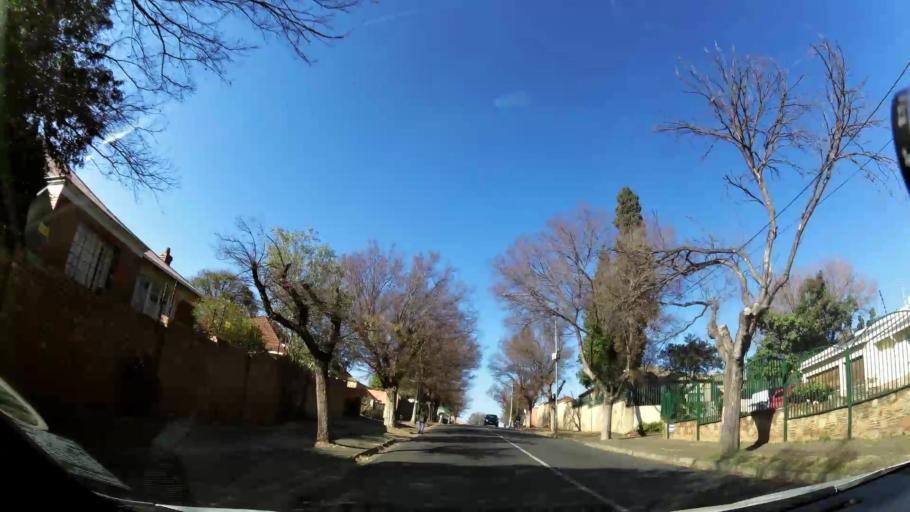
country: ZA
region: Gauteng
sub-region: City of Johannesburg Metropolitan Municipality
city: Johannesburg
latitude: -26.1992
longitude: 28.0980
